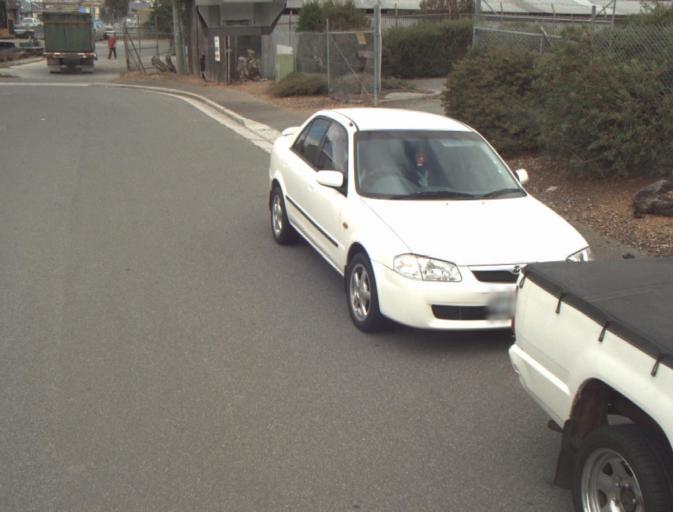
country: AU
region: Tasmania
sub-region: Launceston
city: Launceston
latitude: -41.4227
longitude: 147.1322
